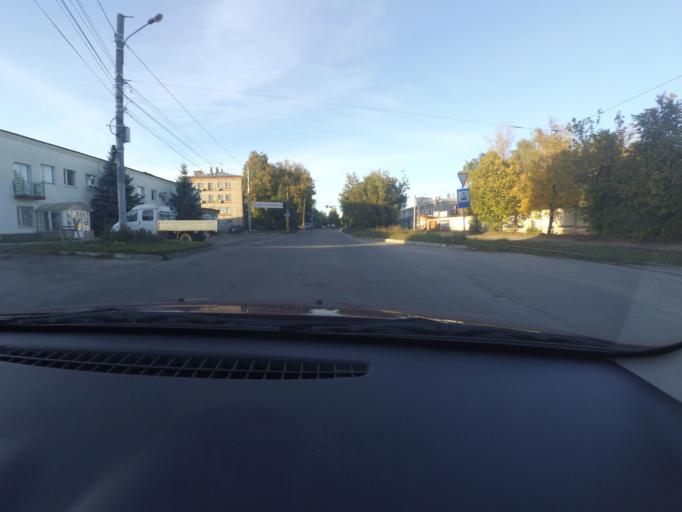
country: RU
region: Nizjnij Novgorod
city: Nizhniy Novgorod
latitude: 56.2841
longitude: 43.9937
